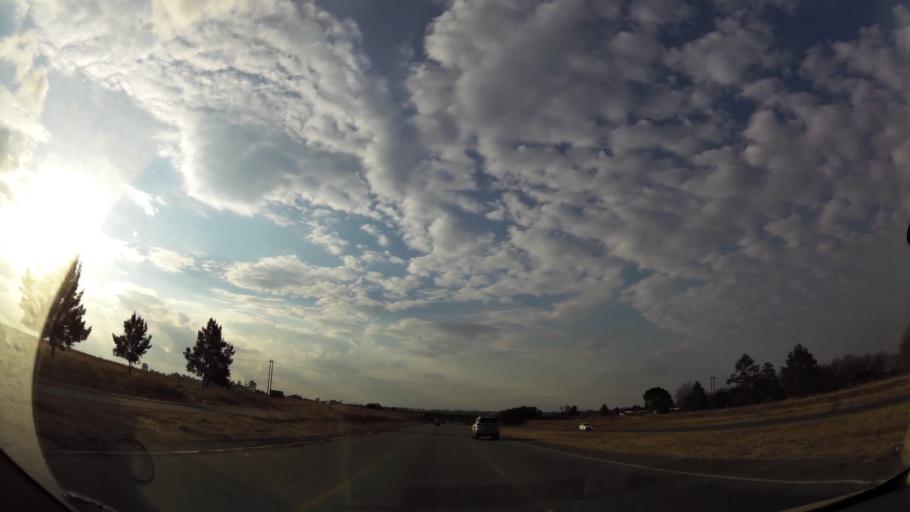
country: ZA
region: Gauteng
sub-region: Sedibeng District Municipality
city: Vanderbijlpark
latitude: -26.7618
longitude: 27.8248
